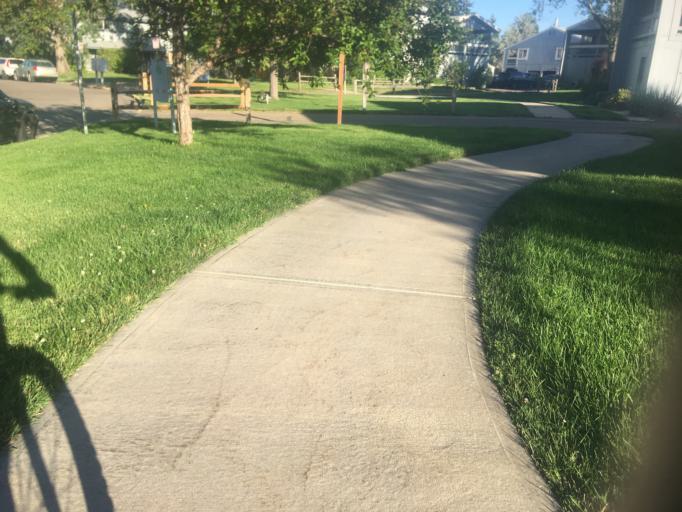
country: US
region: Colorado
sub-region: Boulder County
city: Boulder
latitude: 40.0054
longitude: -105.2426
